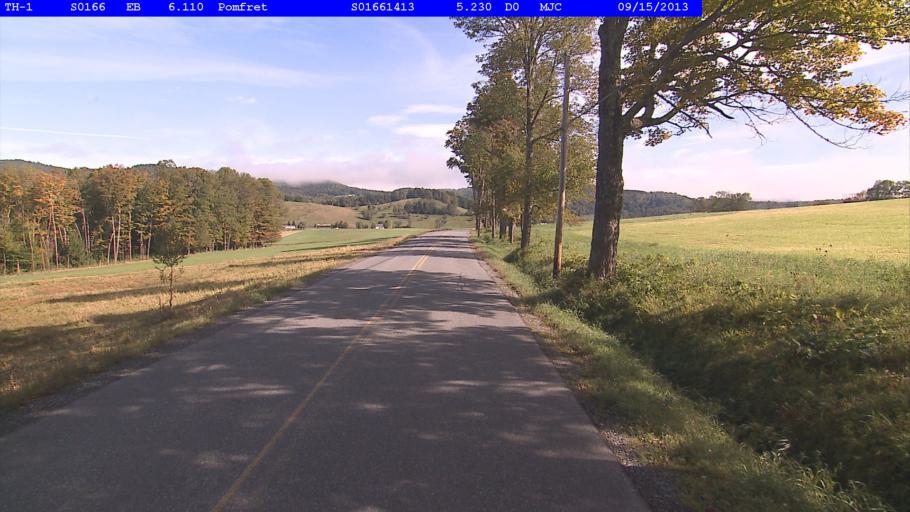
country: US
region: Vermont
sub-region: Windsor County
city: Woodstock
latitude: 43.7158
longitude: -72.5056
